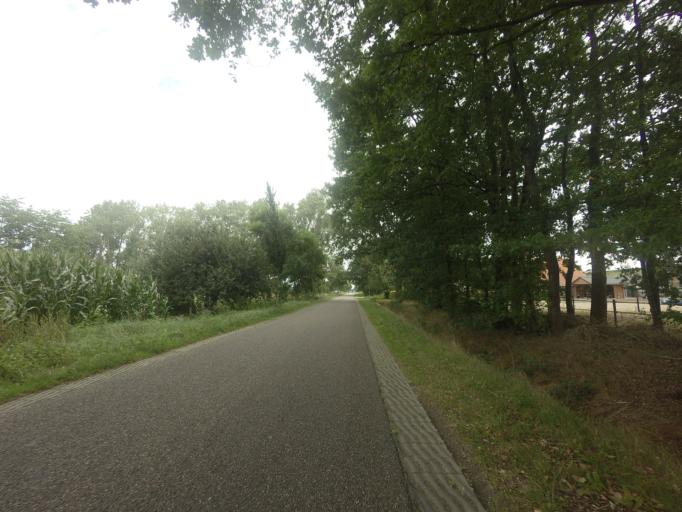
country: NL
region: Overijssel
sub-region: Gemeente Dalfsen
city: Dalfsen
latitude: 52.4782
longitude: 6.3725
